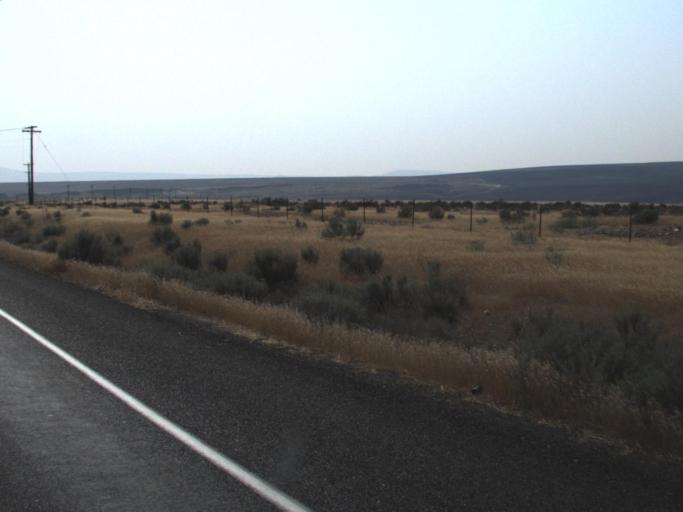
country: US
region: Washington
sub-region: Grant County
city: Desert Aire
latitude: 46.6367
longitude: -119.7289
